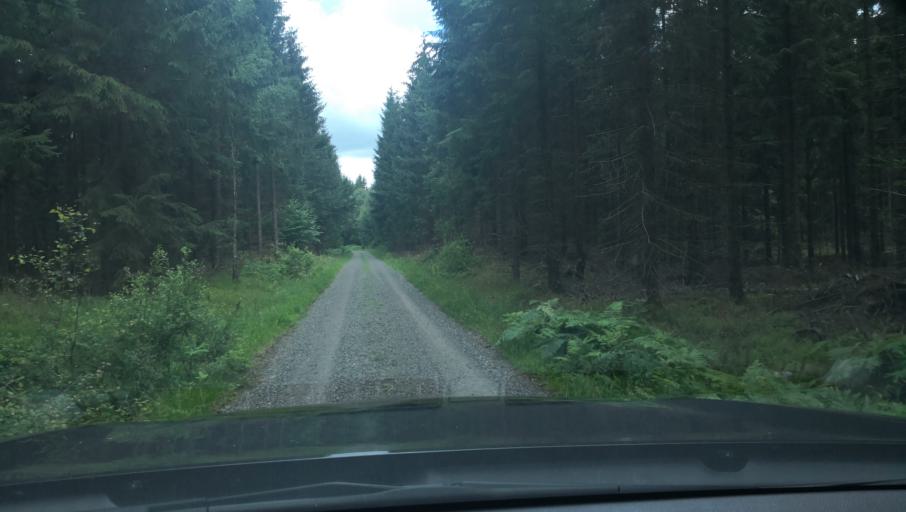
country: SE
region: Skane
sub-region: Simrishamns Kommun
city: Kivik
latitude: 55.6097
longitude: 14.1185
